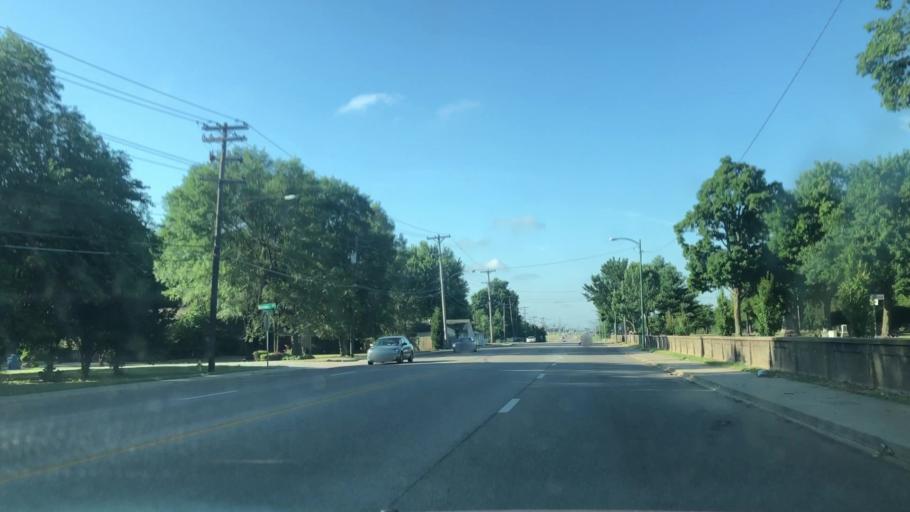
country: US
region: Missouri
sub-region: Greene County
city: Springfield
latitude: 37.1717
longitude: -93.2626
